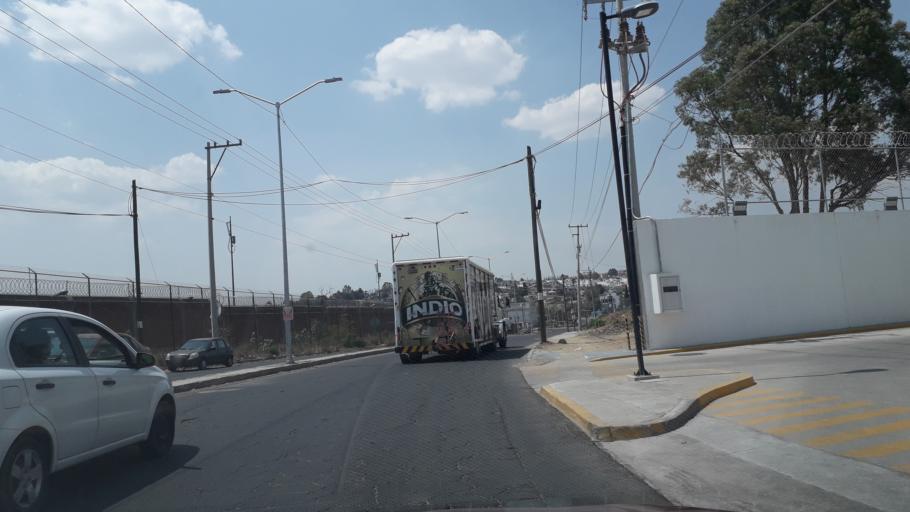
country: MX
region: Puebla
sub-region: Puebla
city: Galaxia la Calera
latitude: 18.9919
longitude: -98.1714
